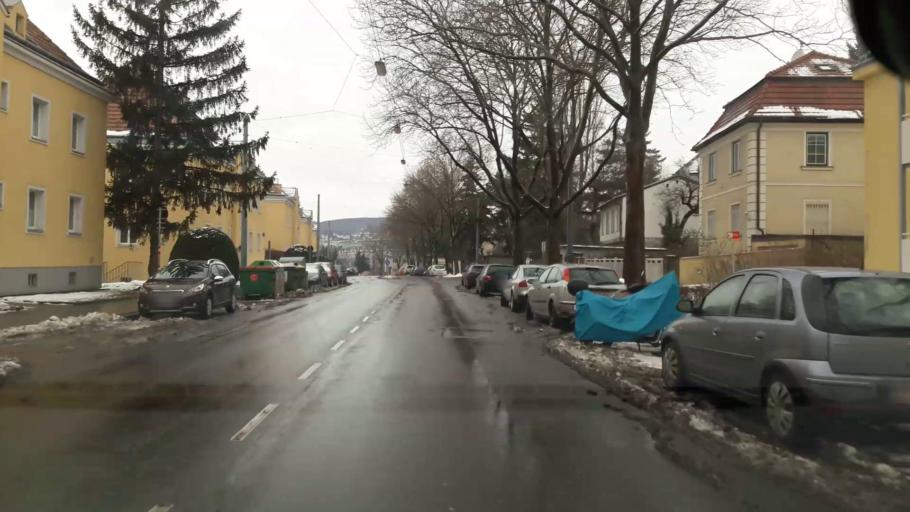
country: AT
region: Lower Austria
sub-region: Politischer Bezirk Modling
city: Perchtoldsdorf
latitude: 48.1727
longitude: 16.2923
